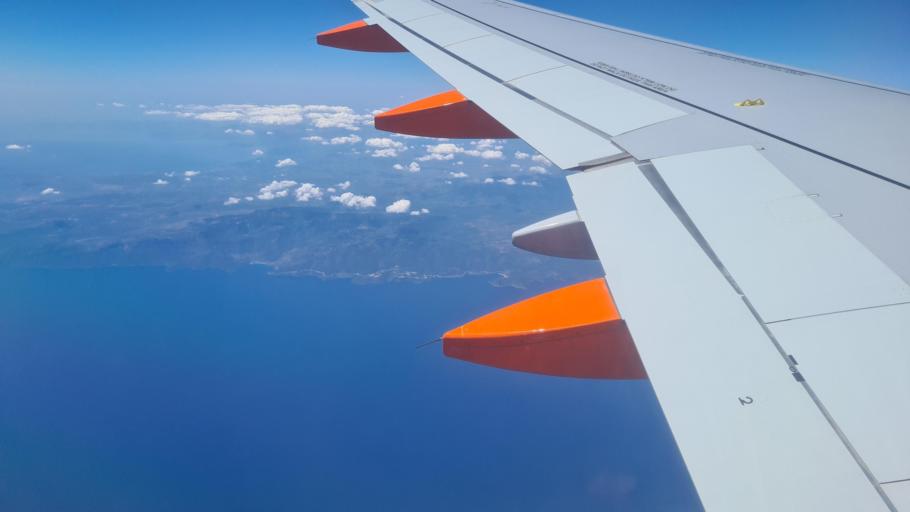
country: GR
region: Peloponnese
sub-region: Nomos Lakonias
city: Gefyra
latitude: 36.8427
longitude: 23.3509
